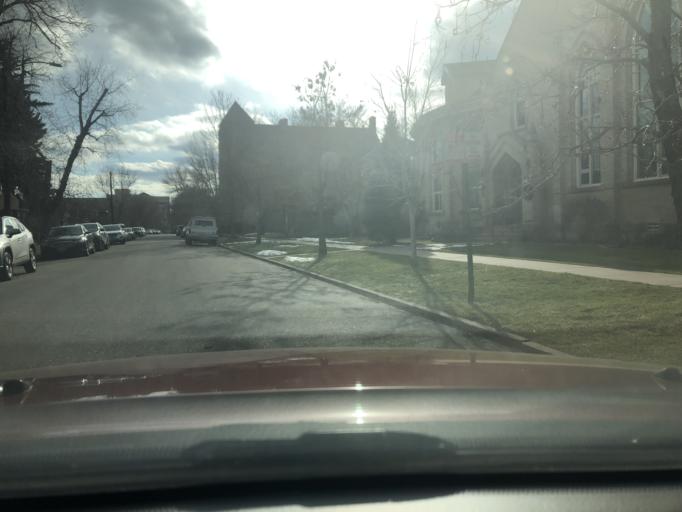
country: US
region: Colorado
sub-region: Denver County
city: Denver
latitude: 39.7507
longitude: -104.9746
